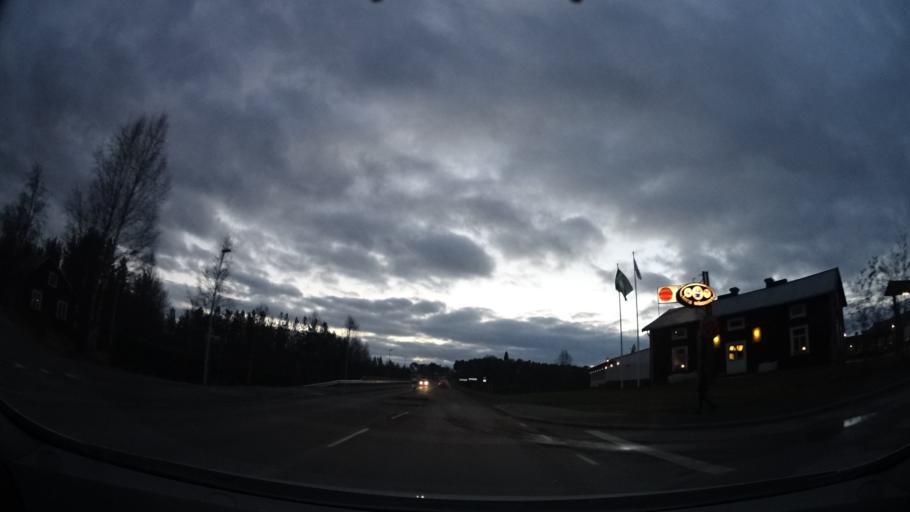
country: SE
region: Vaesterbotten
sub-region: Asele Kommun
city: Asele
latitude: 64.1674
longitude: 17.3685
